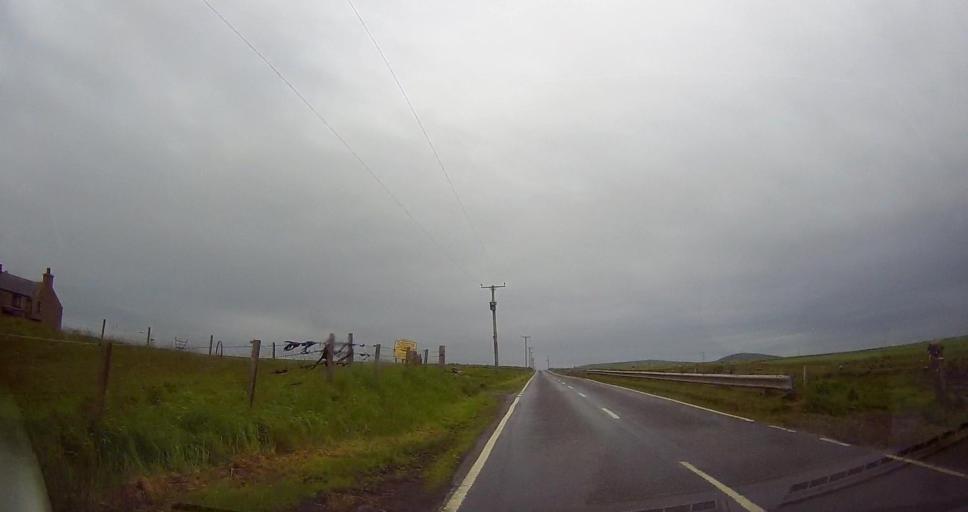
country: GB
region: Scotland
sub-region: Orkney Islands
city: Stromness
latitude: 59.0260
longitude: -3.2937
